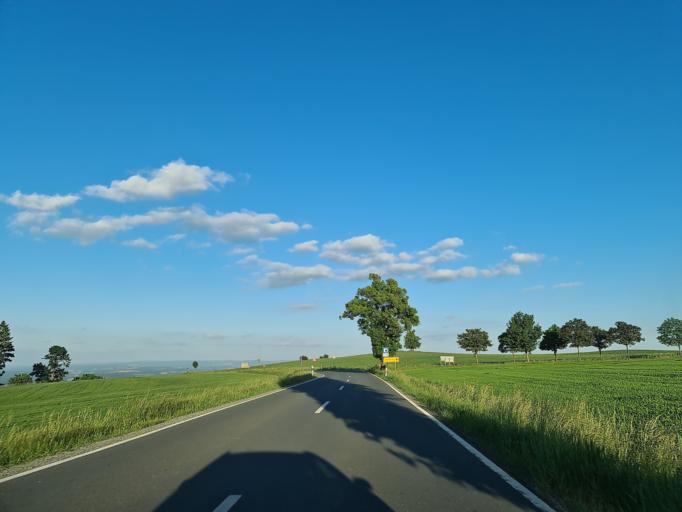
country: DE
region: Saxony
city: Reuth
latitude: 50.4740
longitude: 11.9631
